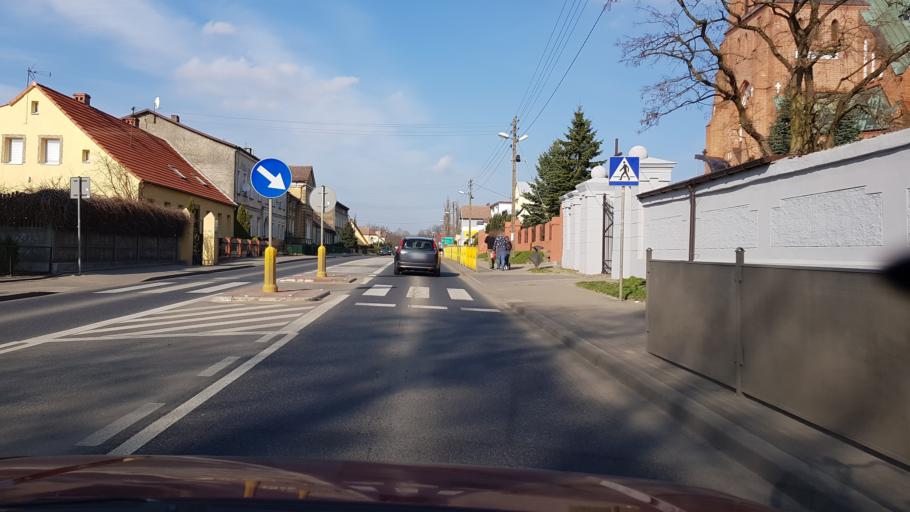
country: PL
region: West Pomeranian Voivodeship
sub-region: Powiat gryficki
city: Ploty
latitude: 53.8029
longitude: 15.2688
